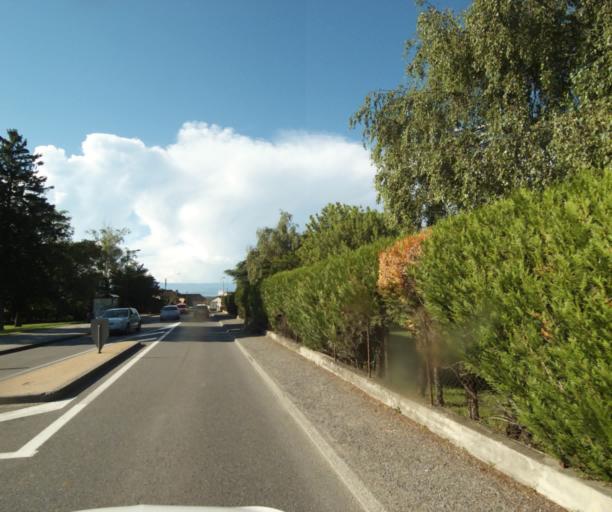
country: FR
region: Rhone-Alpes
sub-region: Departement de la Haute-Savoie
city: Loisin
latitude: 46.2897
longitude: 6.3095
